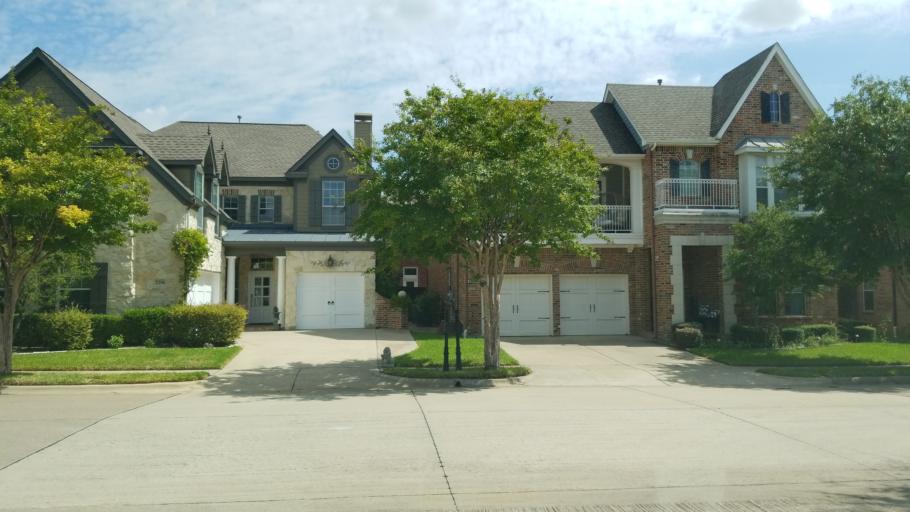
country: US
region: Texas
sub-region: Tarrant County
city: Euless
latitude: 32.8694
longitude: -97.0935
